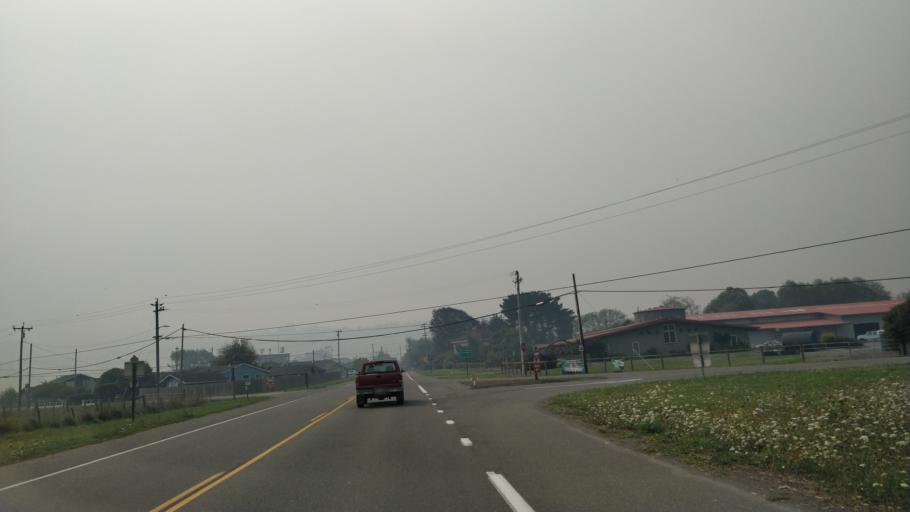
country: US
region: California
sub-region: Humboldt County
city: Ferndale
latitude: 40.5896
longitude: -124.2546
